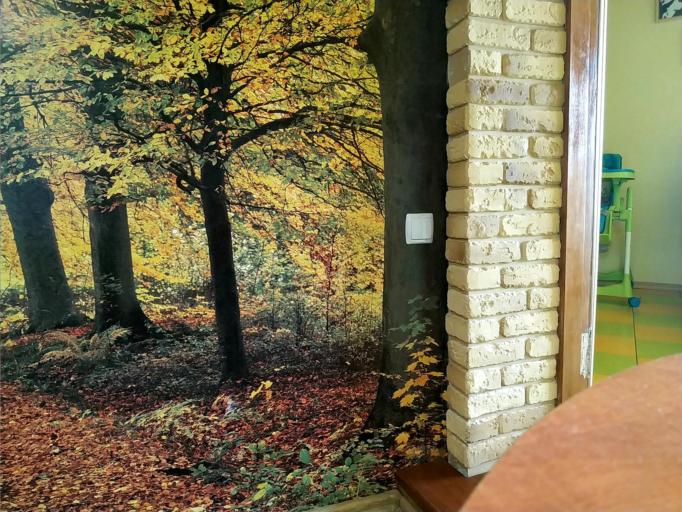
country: RU
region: Smolensk
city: Ozernyy
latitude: 55.4594
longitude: 32.6646
